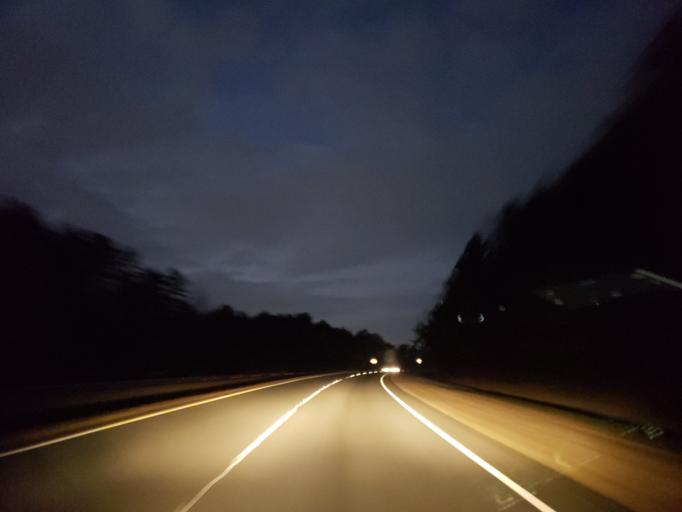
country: US
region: Georgia
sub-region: Polk County
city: Rockmart
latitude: 33.9916
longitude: -85.0247
